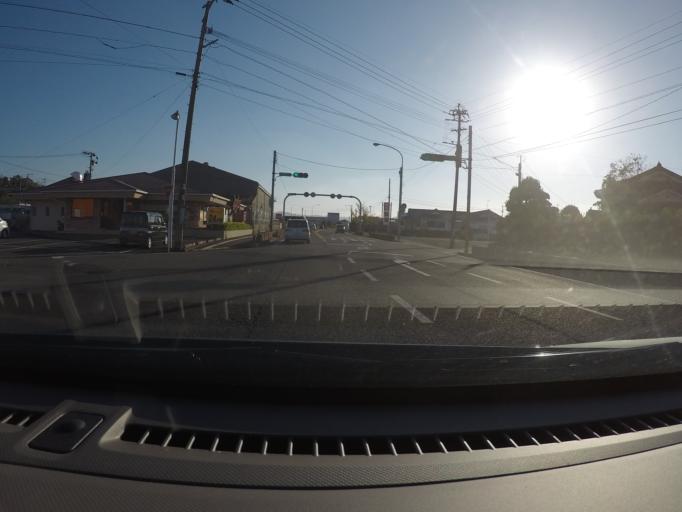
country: JP
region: Kagoshima
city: Izumi
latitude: 32.1240
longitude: 130.3422
